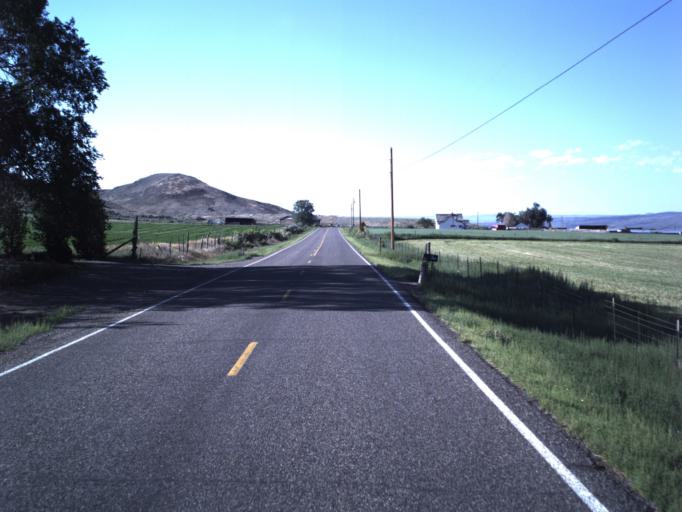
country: US
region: Utah
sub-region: Wayne County
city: Loa
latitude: 38.4438
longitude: -111.6158
